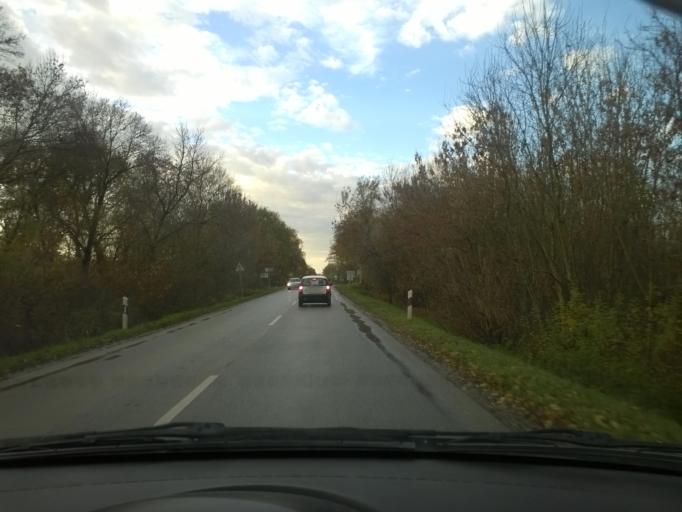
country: HU
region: Bacs-Kiskun
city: Kalocsa
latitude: 46.5159
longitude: 18.9995
